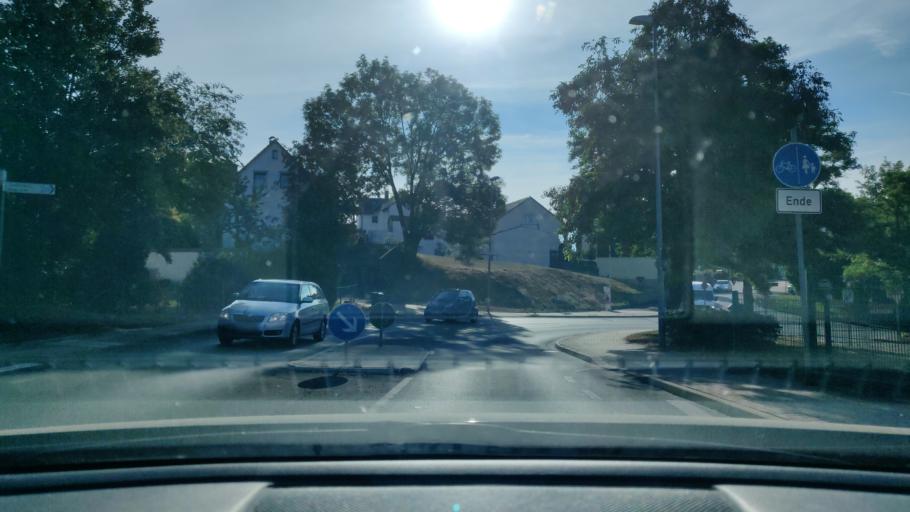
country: DE
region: Hesse
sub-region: Regierungsbezirk Kassel
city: Bad Wildungen
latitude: 51.1283
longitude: 9.1267
